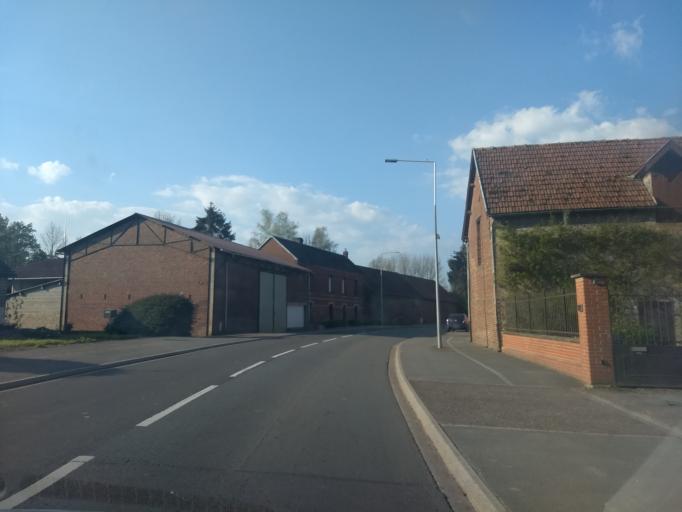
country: FR
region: Nord-Pas-de-Calais
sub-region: Departement du Pas-de-Calais
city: Bucquoy
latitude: 50.1356
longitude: 2.7072
